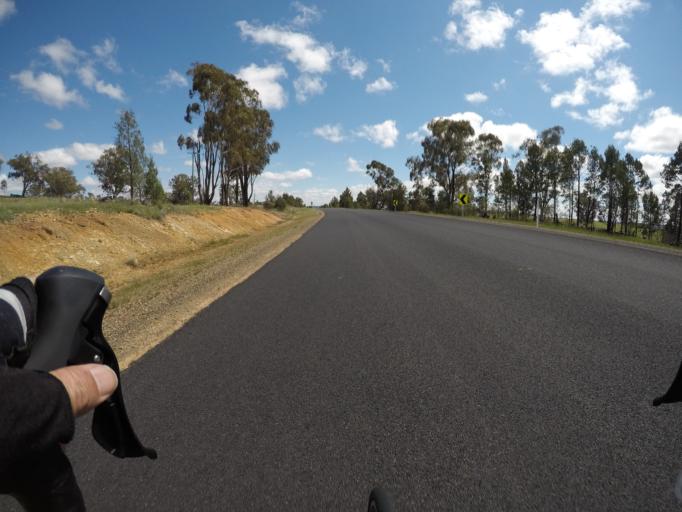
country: AU
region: New South Wales
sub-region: Dubbo Municipality
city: Dubbo
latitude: -32.5125
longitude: 148.5552
